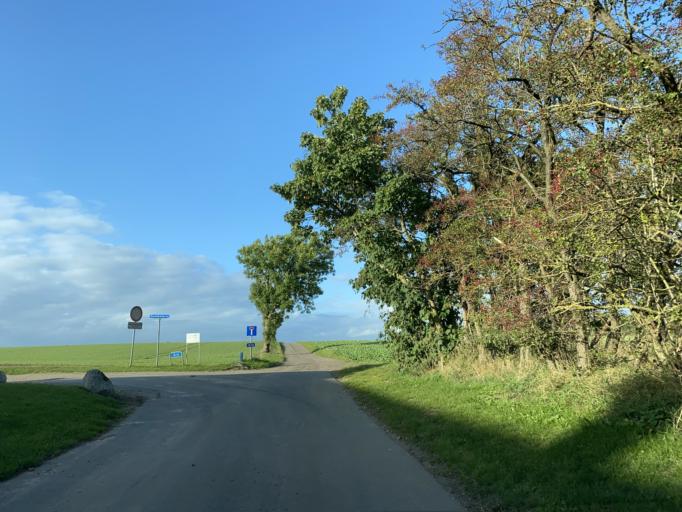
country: DK
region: Central Jutland
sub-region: Skanderborg Kommune
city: Ry
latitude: 56.1569
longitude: 9.8079
